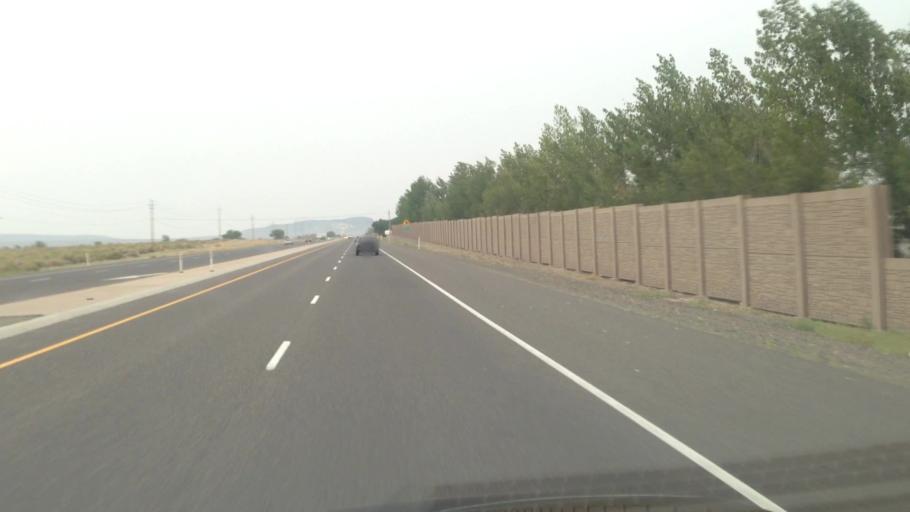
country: US
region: Nevada
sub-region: Lyon County
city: Fernley
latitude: 39.5935
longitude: -119.1612
